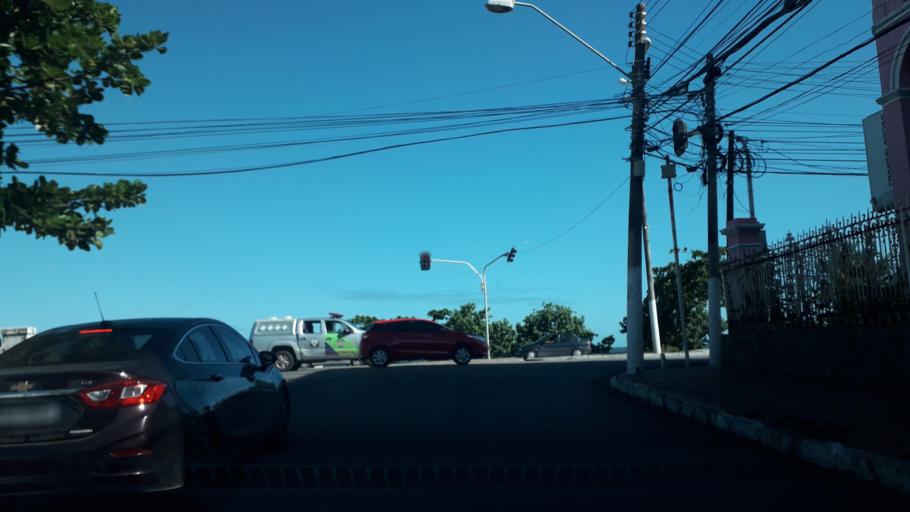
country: BR
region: Alagoas
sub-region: Maceio
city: Maceio
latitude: -9.6695
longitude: -35.7309
